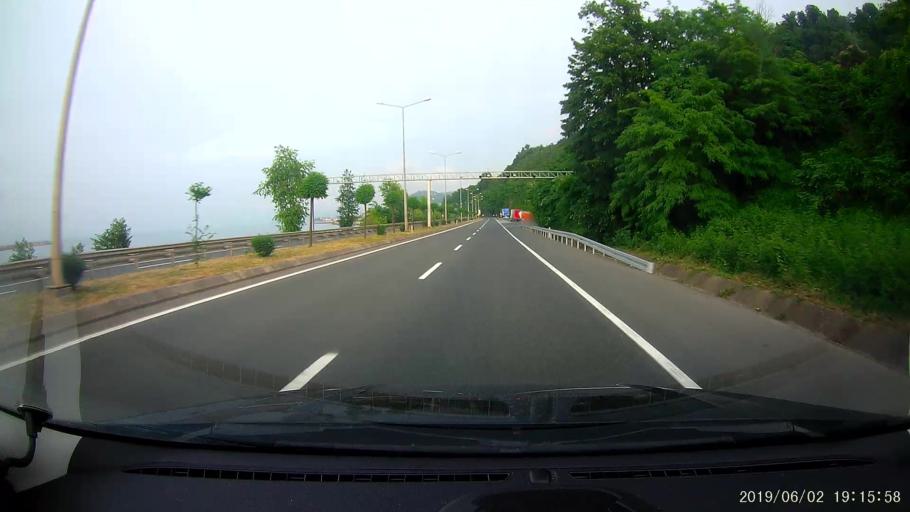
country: TR
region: Giresun
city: Piraziz
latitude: 40.9599
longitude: 38.1063
